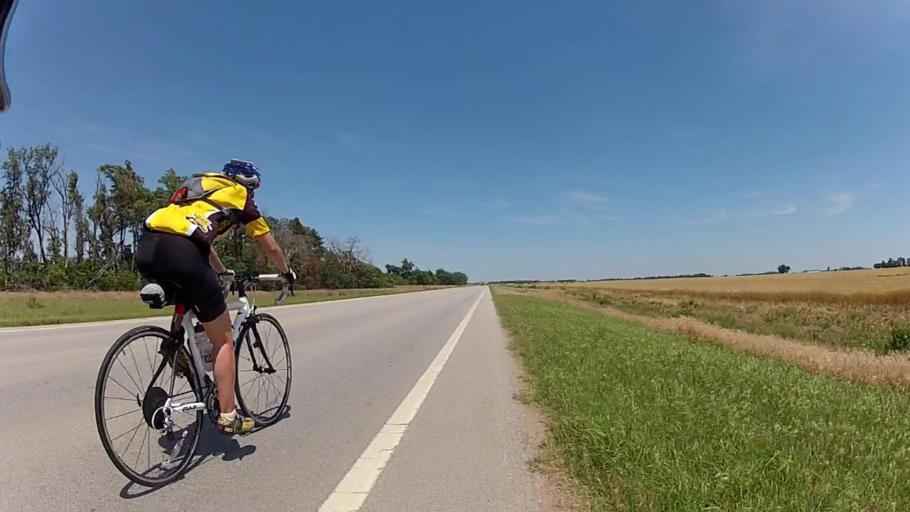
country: US
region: Kansas
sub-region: Harper County
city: Harper
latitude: 37.2388
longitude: -98.1552
